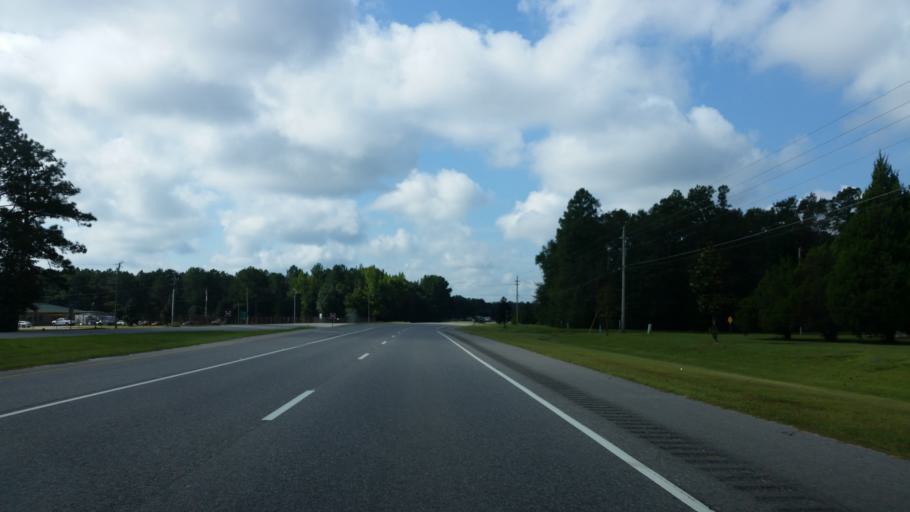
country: US
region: Alabama
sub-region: Baldwin County
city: Bay Minette
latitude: 30.9185
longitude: -87.7761
